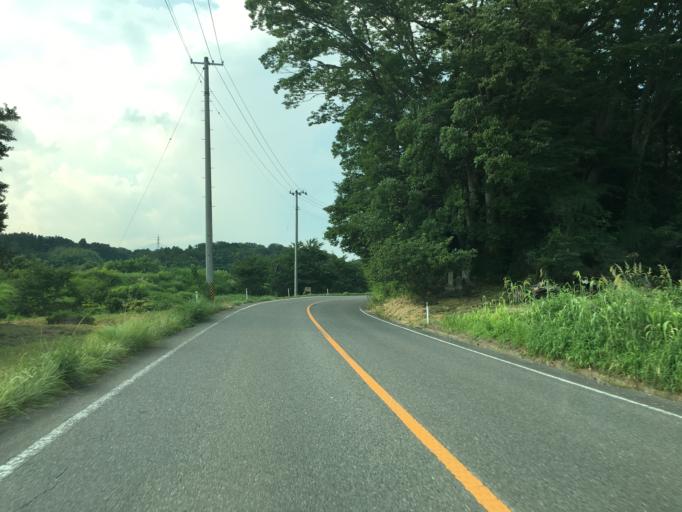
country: JP
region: Fukushima
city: Motomiya
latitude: 37.4786
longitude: 140.4143
